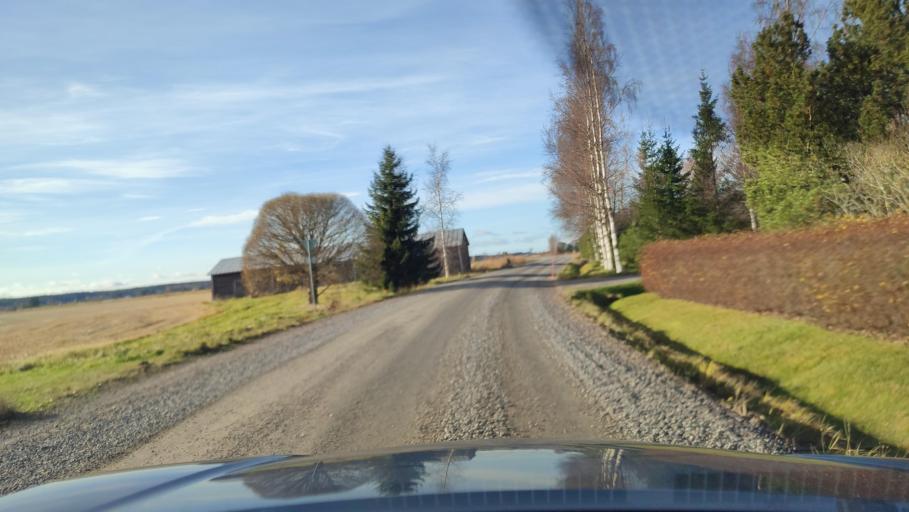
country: FI
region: Southern Ostrobothnia
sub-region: Suupohja
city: Teuva
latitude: 62.4673
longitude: 21.7095
